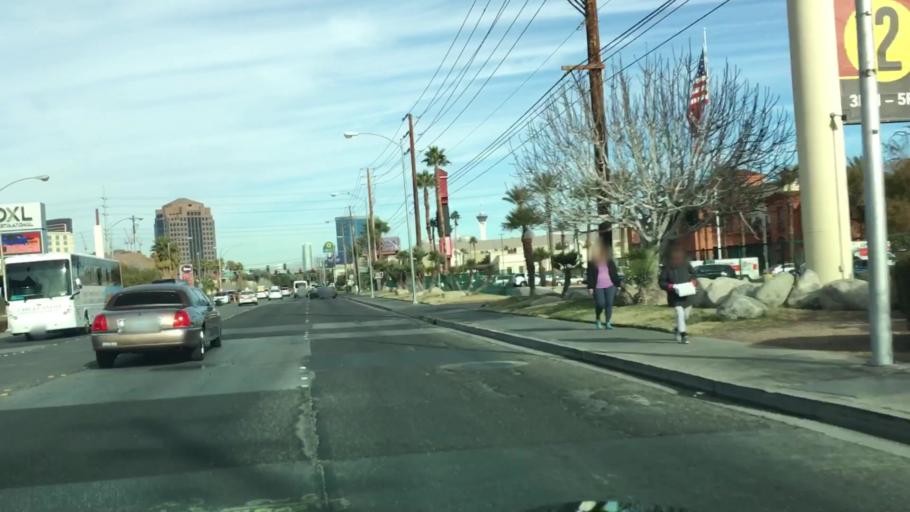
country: US
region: Nevada
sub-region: Clark County
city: Paradise
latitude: 36.1124
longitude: -115.1534
